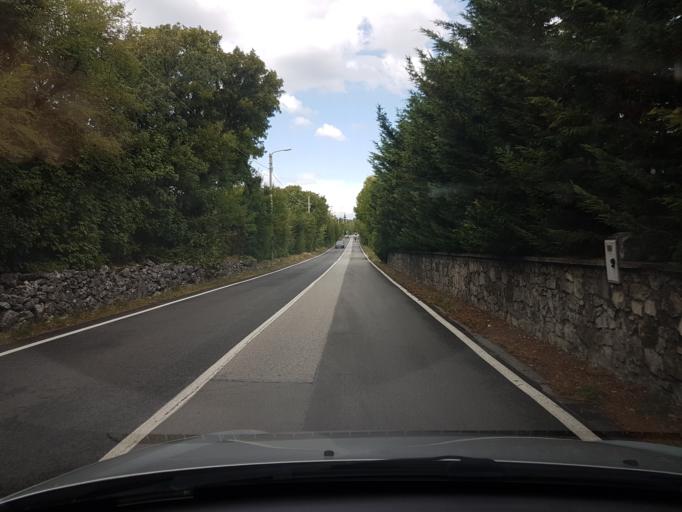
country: IT
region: Friuli Venezia Giulia
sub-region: Provincia di Trieste
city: Prosecco-Contovello
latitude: 45.7097
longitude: 13.7295
